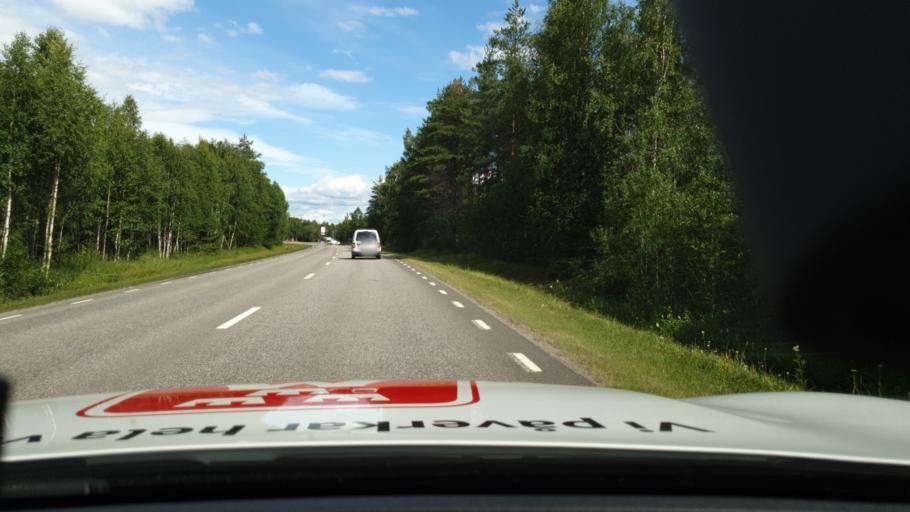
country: SE
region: Norrbotten
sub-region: Lulea Kommun
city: Ranea
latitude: 65.8471
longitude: 22.2707
